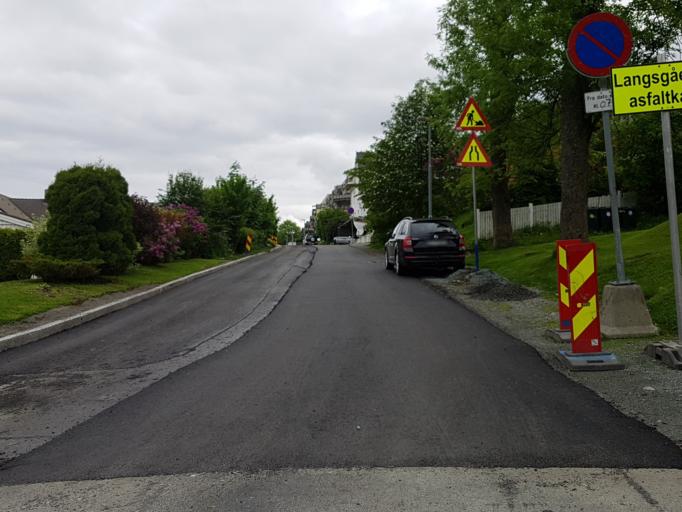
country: NO
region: Sor-Trondelag
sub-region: Trondheim
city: Trondheim
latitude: 63.4367
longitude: 10.4422
